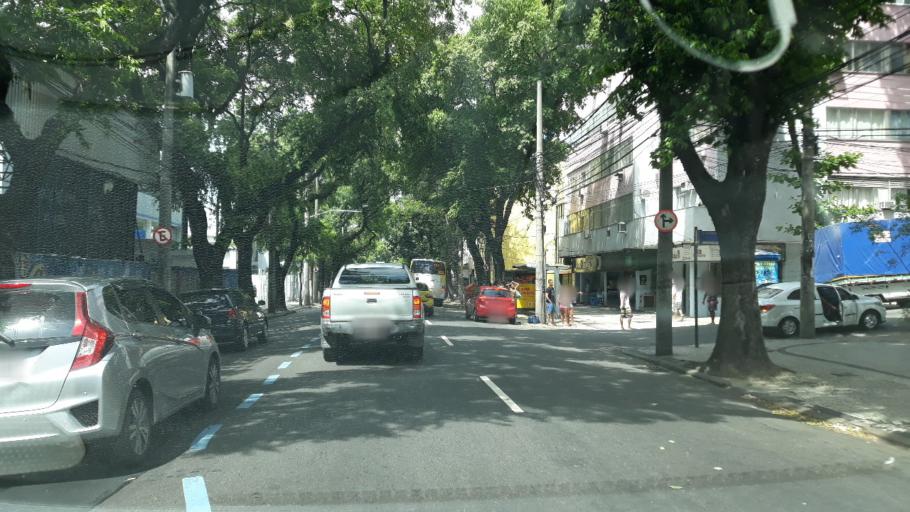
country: BR
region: Rio de Janeiro
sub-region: Rio De Janeiro
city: Rio de Janeiro
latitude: -22.9158
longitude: -43.2084
